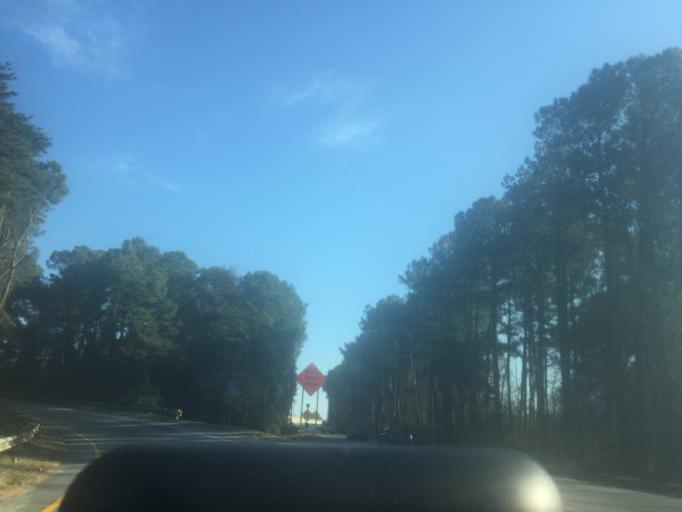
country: US
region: Georgia
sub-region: Clayton County
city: Forest Park
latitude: 33.6148
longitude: -84.3995
